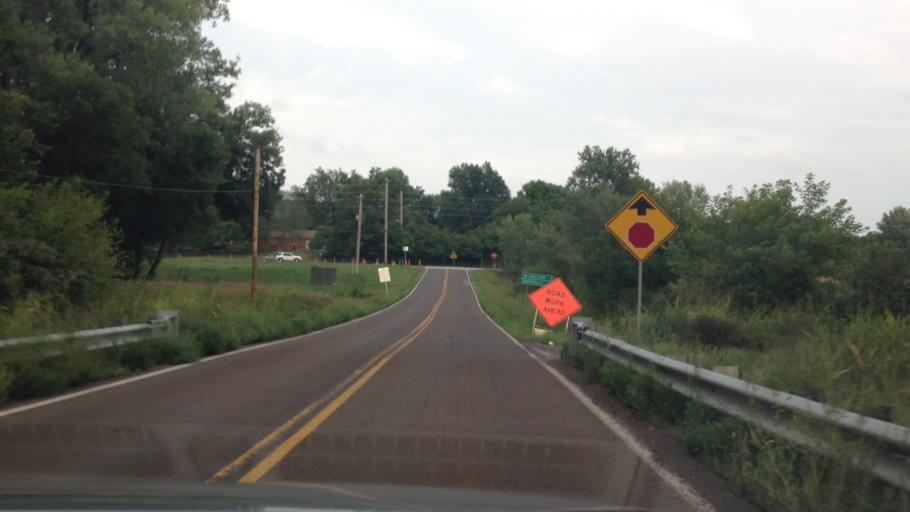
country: US
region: Missouri
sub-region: Clay County
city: Smithville
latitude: 39.3978
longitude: -94.5856
